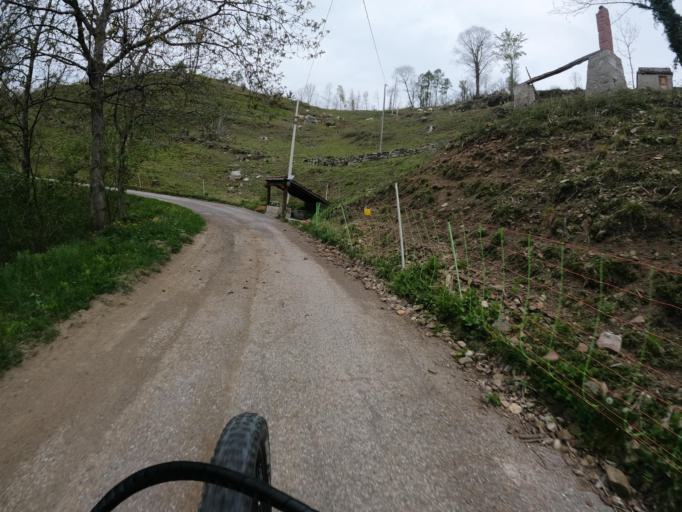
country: IT
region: Friuli Venezia Giulia
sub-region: Provincia di Udine
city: Clodig
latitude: 46.1274
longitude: 13.6127
